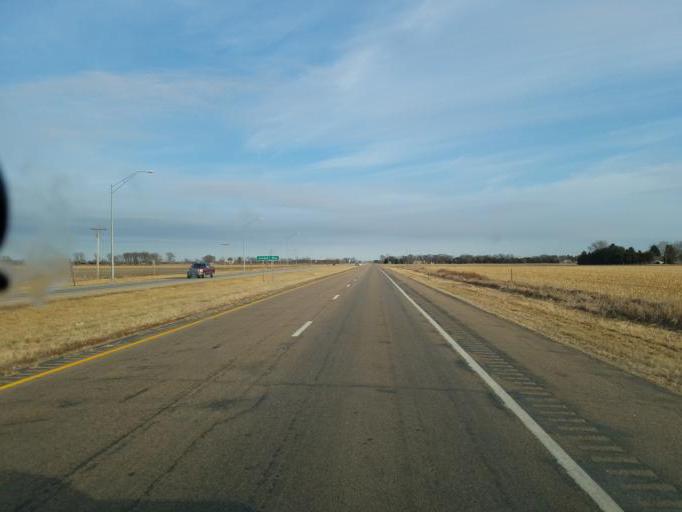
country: US
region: South Dakota
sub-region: Union County
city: Dakota Dunes
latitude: 42.4483
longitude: -96.5407
